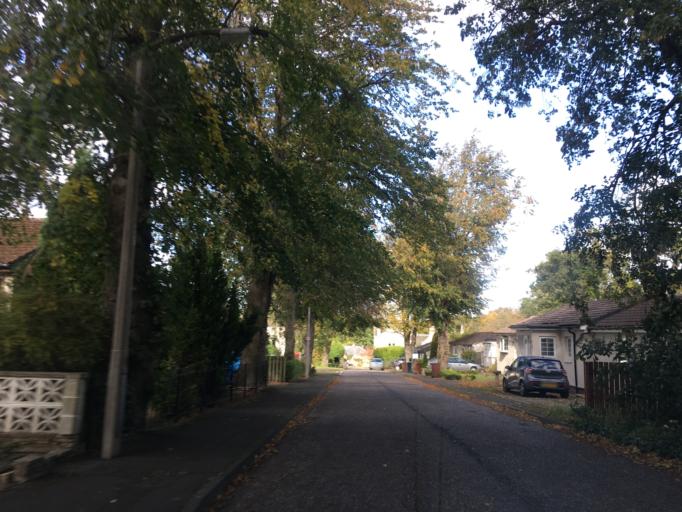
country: GB
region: Scotland
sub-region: Edinburgh
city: Currie
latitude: 55.9639
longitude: -3.3099
